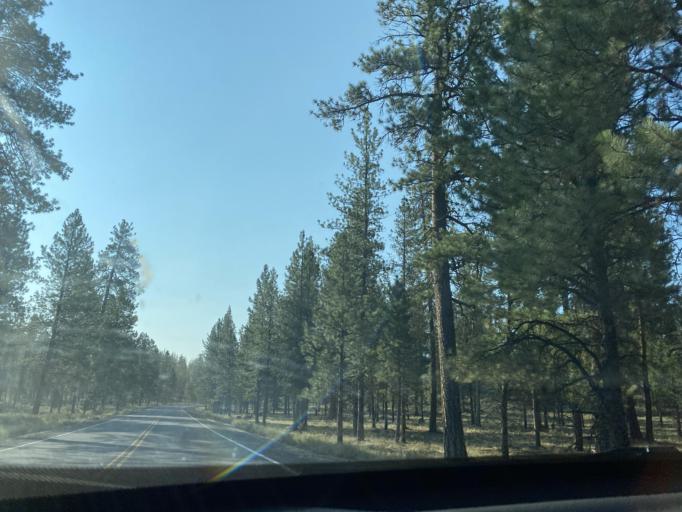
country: US
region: Oregon
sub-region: Deschutes County
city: La Pine
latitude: 43.7111
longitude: -121.4098
